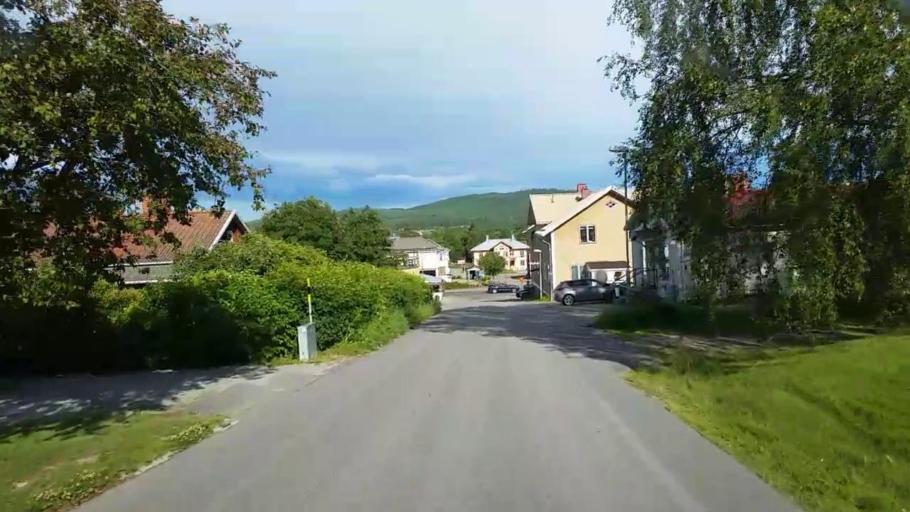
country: SE
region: Gaevleborg
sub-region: Ljusdals Kommun
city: Jaervsoe
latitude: 61.7162
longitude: 16.1675
